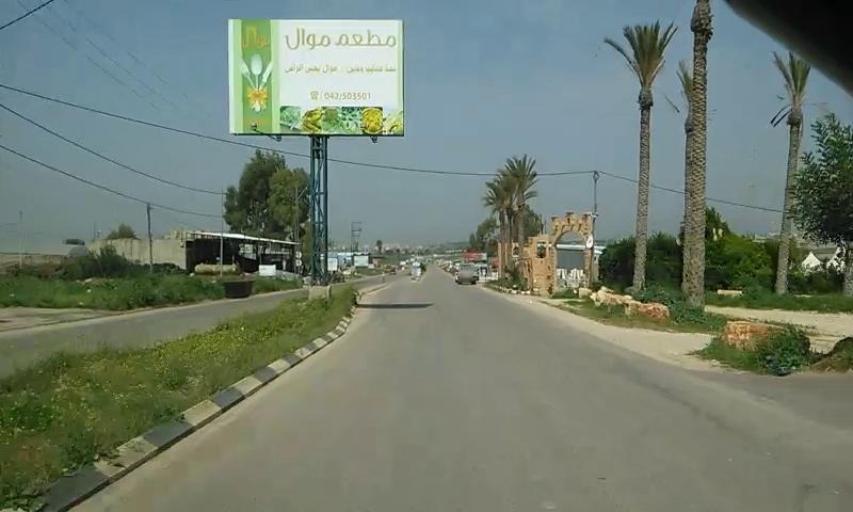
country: PS
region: West Bank
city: Al Jalamah
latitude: 32.4935
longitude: 35.3019
